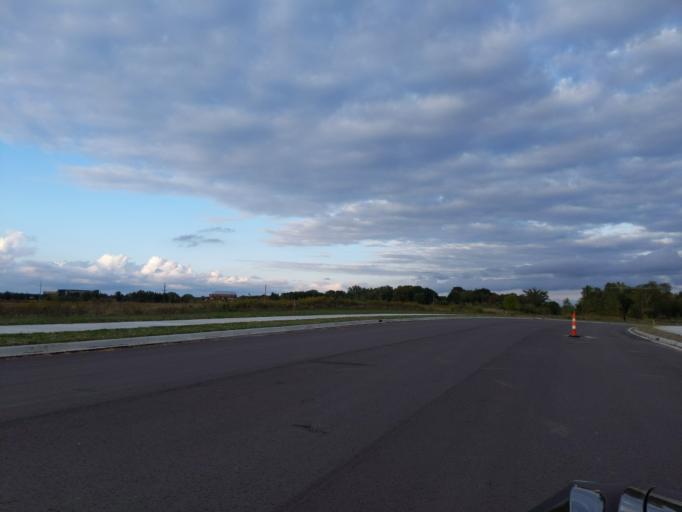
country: US
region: Michigan
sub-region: Ingham County
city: East Lansing
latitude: 42.7729
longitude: -84.5115
